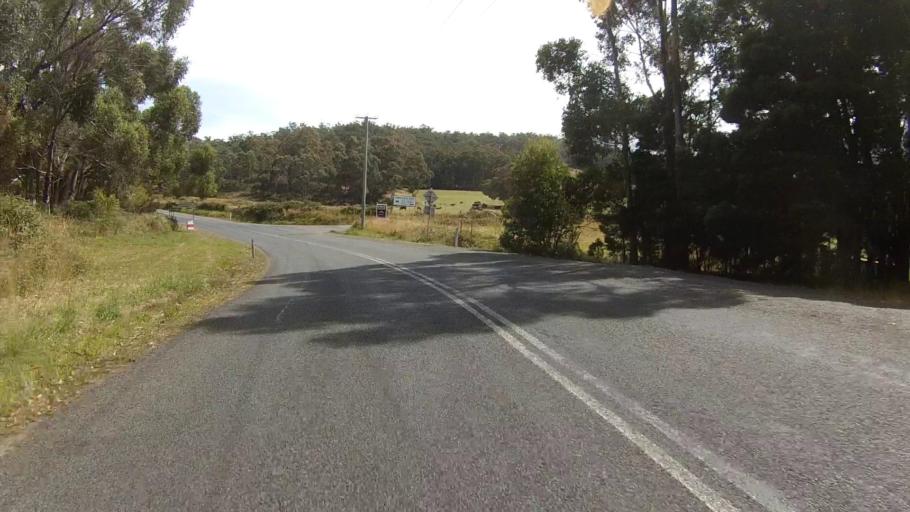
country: AU
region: Tasmania
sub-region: Huon Valley
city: Cygnet
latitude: -43.1850
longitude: 147.1074
